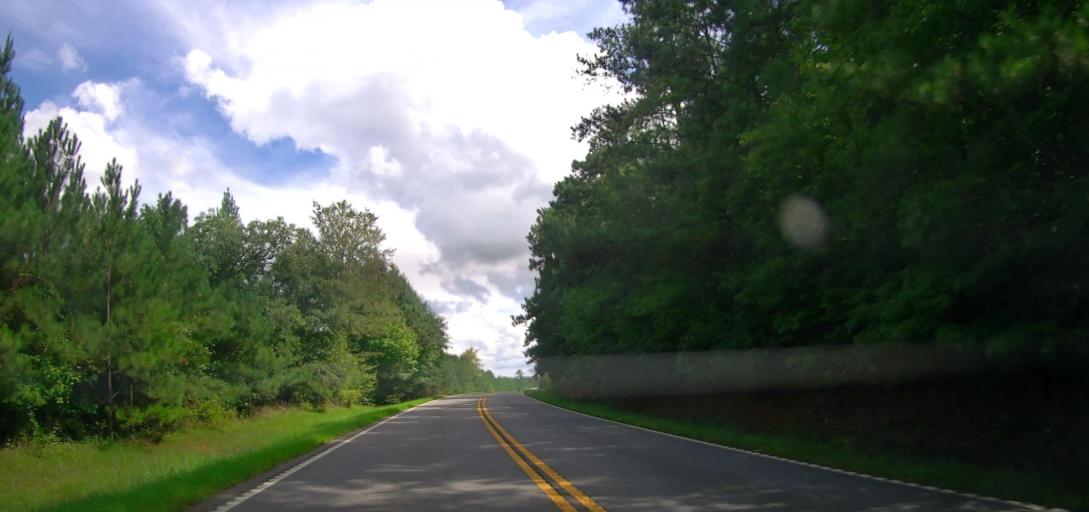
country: US
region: Georgia
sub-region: Talbot County
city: Talbotton
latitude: 32.6636
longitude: -84.5149
